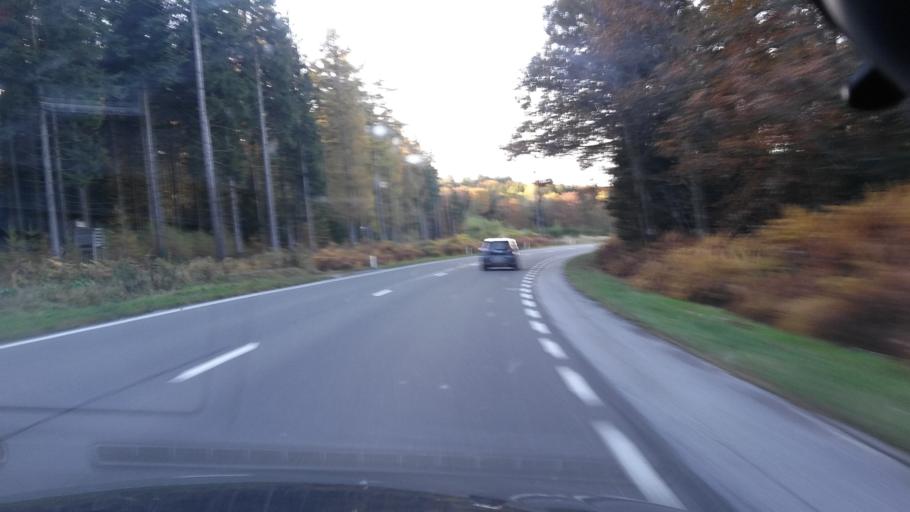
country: BE
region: Wallonia
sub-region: Province du Luxembourg
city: Bouillon
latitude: 49.7591
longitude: 5.1390
